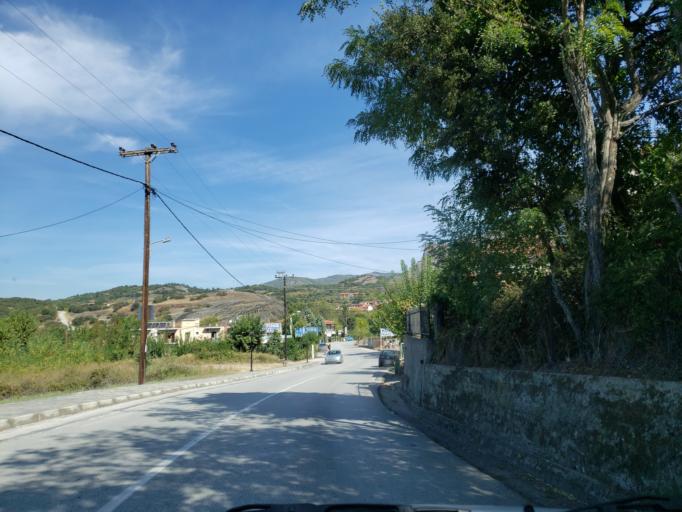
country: GR
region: Thessaly
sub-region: Trikala
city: Kastraki
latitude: 39.7125
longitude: 21.6159
